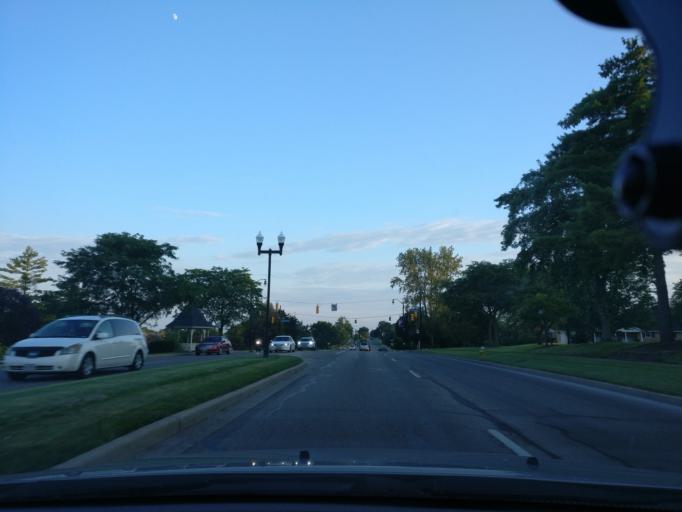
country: US
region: Ohio
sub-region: Montgomery County
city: Centerville
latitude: 39.6204
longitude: -84.1597
